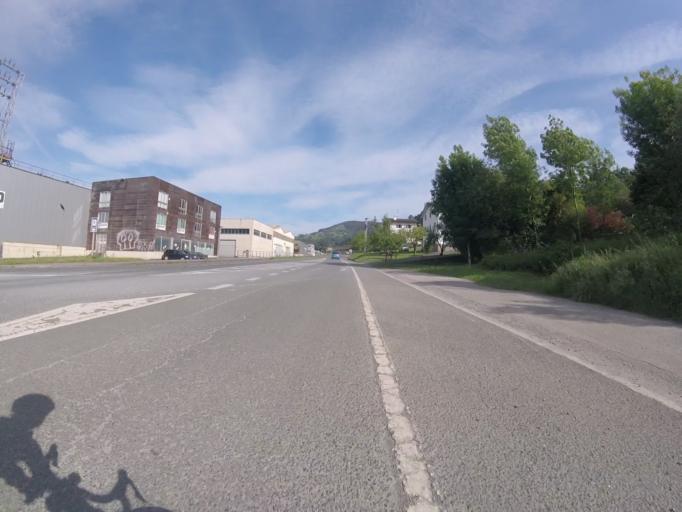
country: ES
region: Basque Country
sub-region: Provincia de Guipuzcoa
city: Gabiria
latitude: 43.0713
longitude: -2.2872
